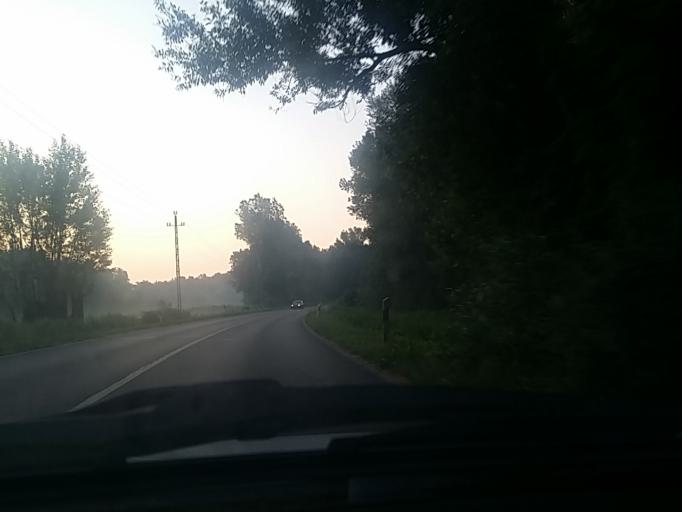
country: HU
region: Budapest
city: Budapest XVII. keruelet
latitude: 47.4891
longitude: 19.2221
